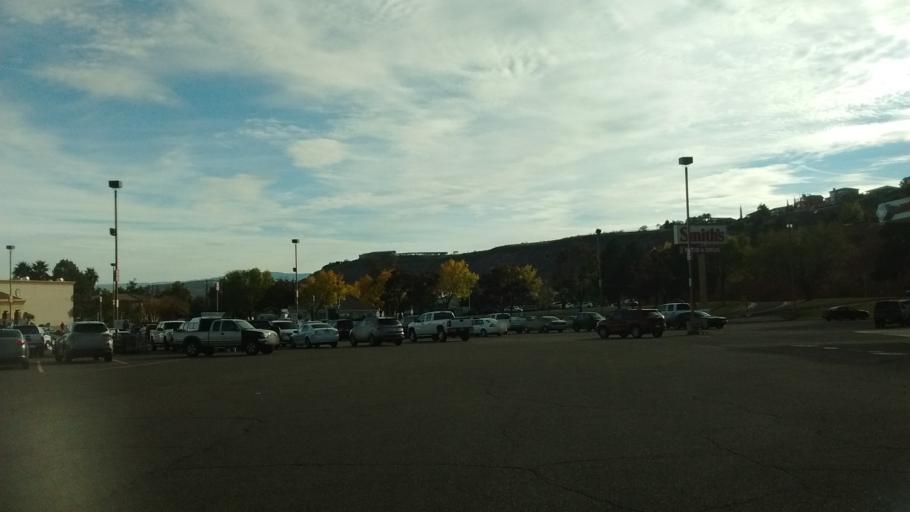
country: US
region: Utah
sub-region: Washington County
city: Saint George
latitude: 37.1097
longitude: -113.5927
